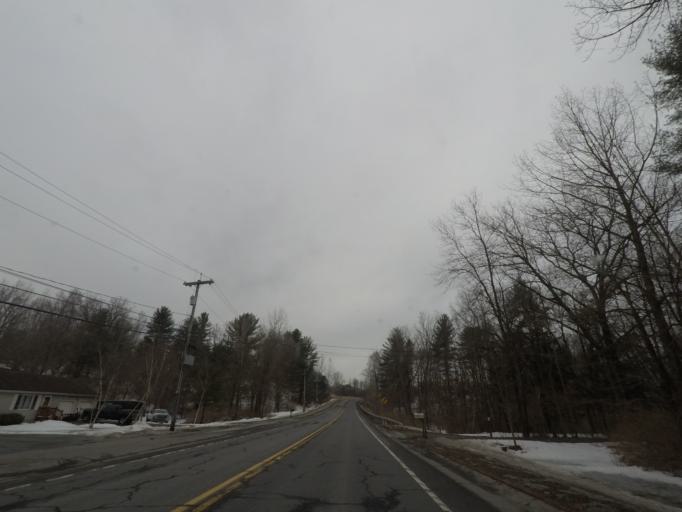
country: US
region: New York
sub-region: Albany County
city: Westmere
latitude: 42.6864
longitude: -73.9013
